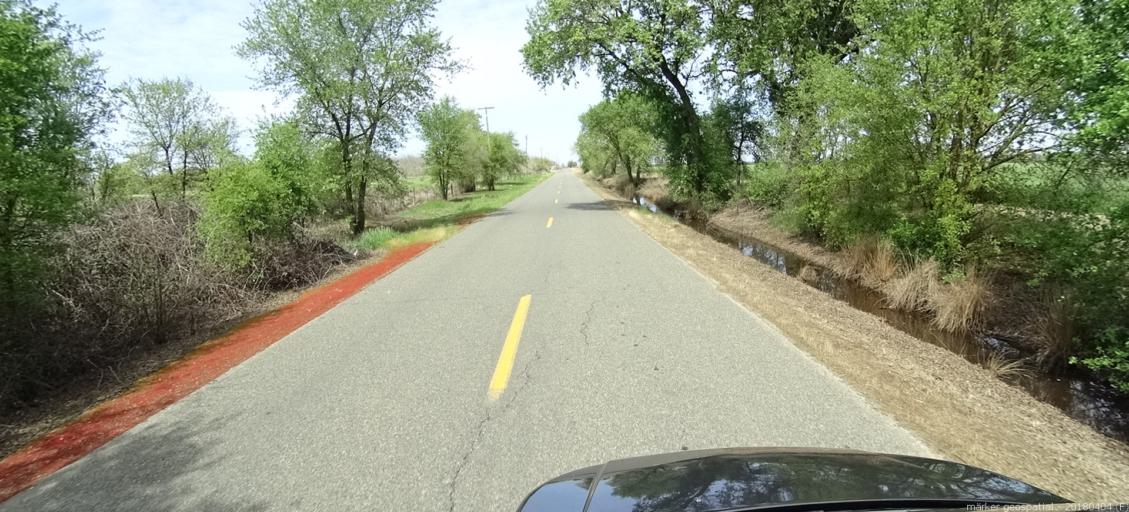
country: US
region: California
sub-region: Sacramento County
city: Herald
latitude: 38.2756
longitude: -121.2082
